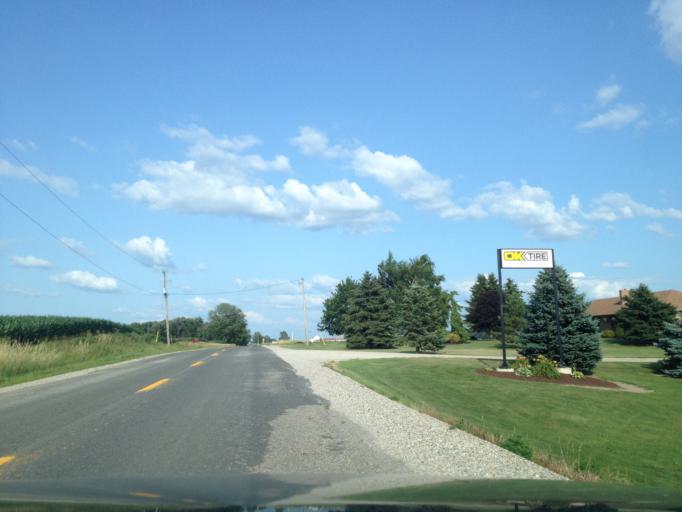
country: CA
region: Ontario
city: Ingersoll
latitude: 42.9624
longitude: -80.7663
